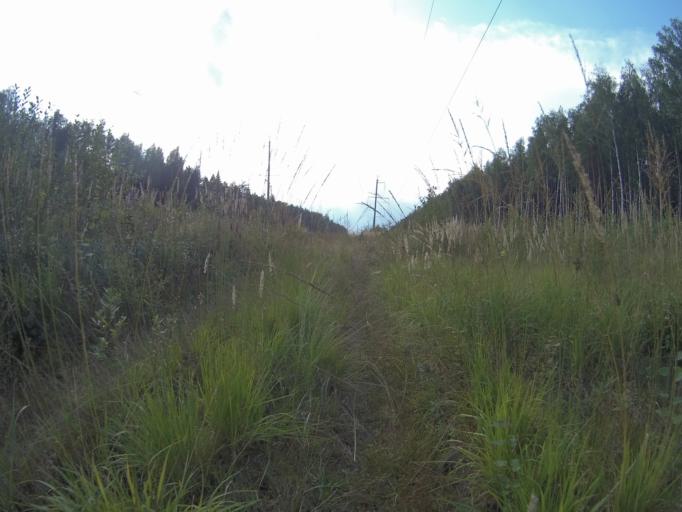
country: RU
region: Vladimir
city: Raduzhnyy
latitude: 56.0135
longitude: 40.2861
